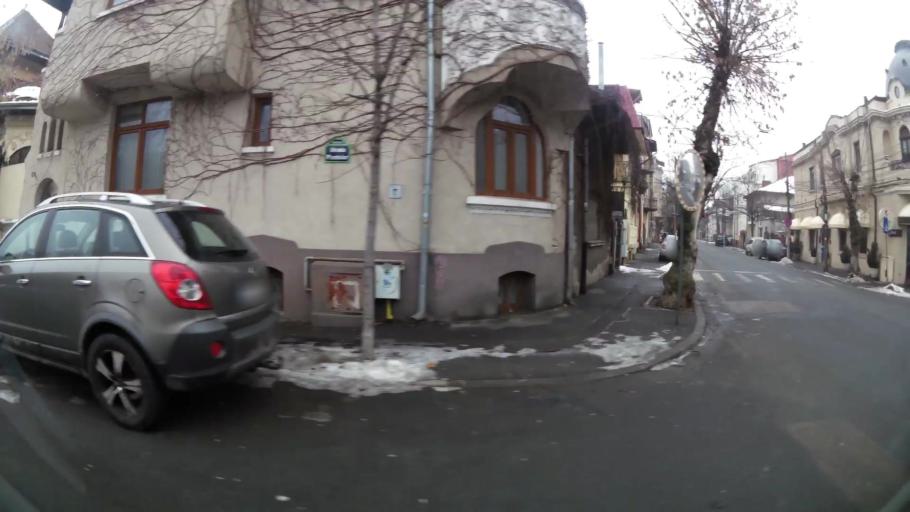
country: RO
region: Bucuresti
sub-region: Municipiul Bucuresti
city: Bucharest
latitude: 44.4364
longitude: 26.1169
